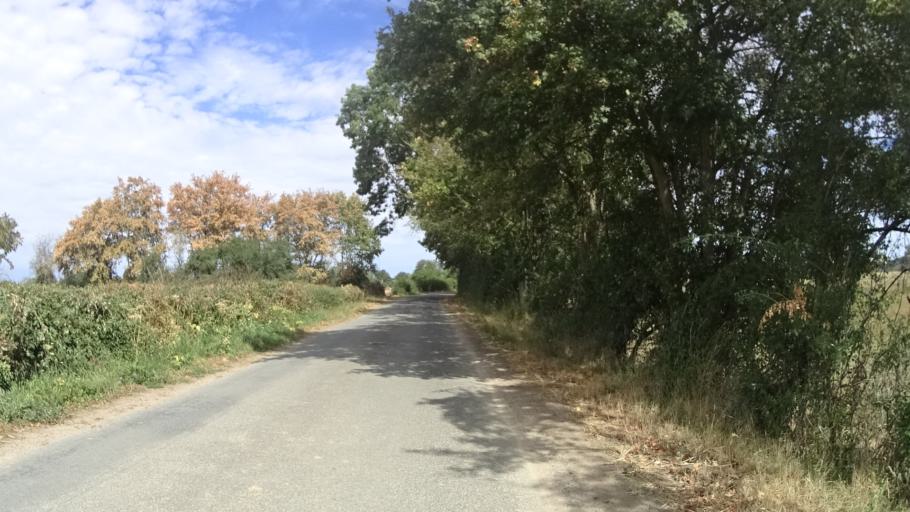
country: FR
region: Auvergne
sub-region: Departement de l'Allier
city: Beaulon
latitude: 46.6459
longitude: 3.6906
